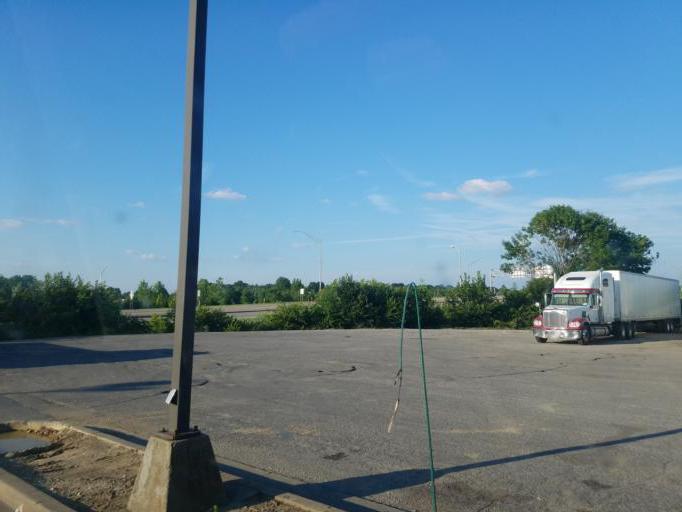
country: US
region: Kentucky
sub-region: Jefferson County
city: Heritage Creek
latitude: 38.1363
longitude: -85.7116
